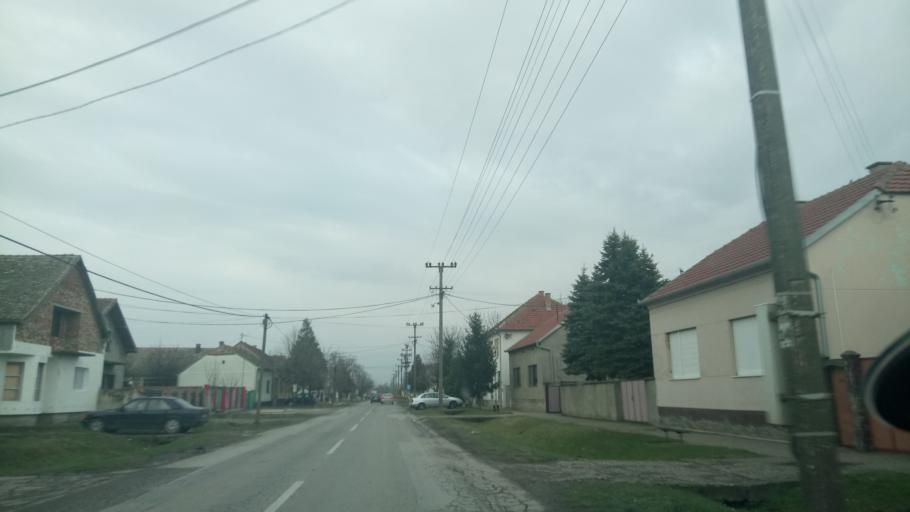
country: RS
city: Vojka
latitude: 44.9405
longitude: 20.1527
